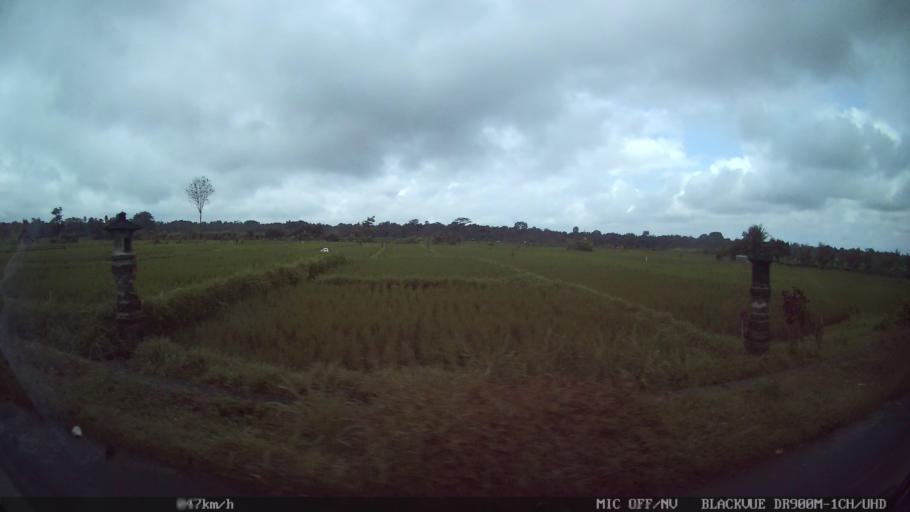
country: ID
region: Bali
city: Banjar Teguan
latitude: -8.4990
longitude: 115.2255
